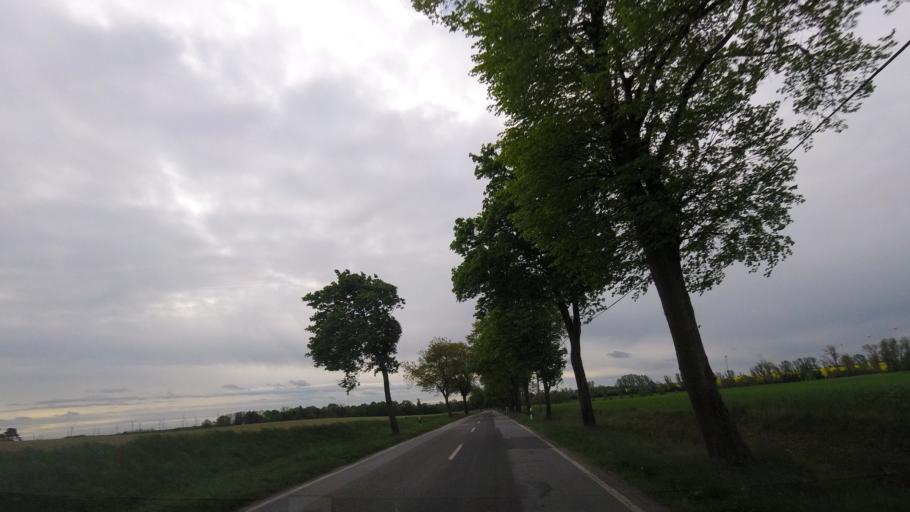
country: DE
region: Brandenburg
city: Dahme
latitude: 51.8925
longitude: 13.4136
